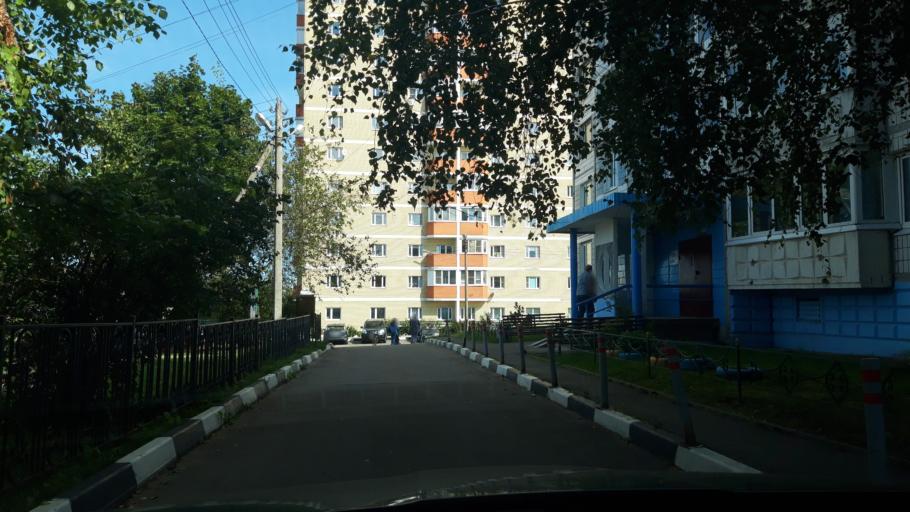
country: RU
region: Moskovskaya
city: Chashnikovo
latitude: 56.0304
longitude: 37.1707
